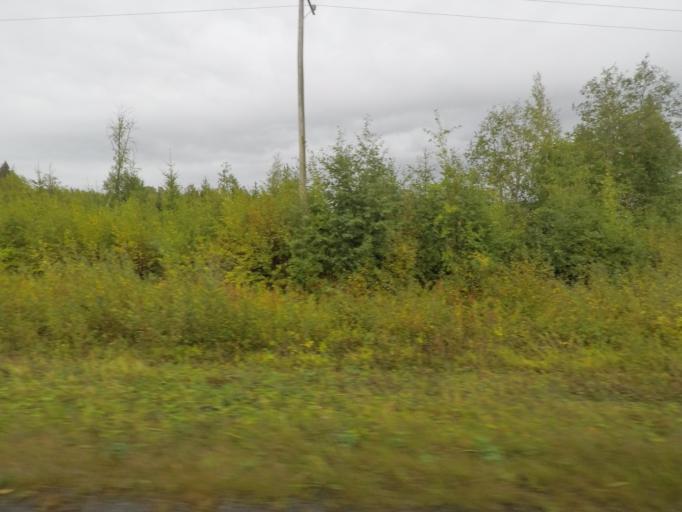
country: FI
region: Southern Savonia
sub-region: Pieksaemaeki
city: Juva
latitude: 61.9326
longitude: 27.8062
